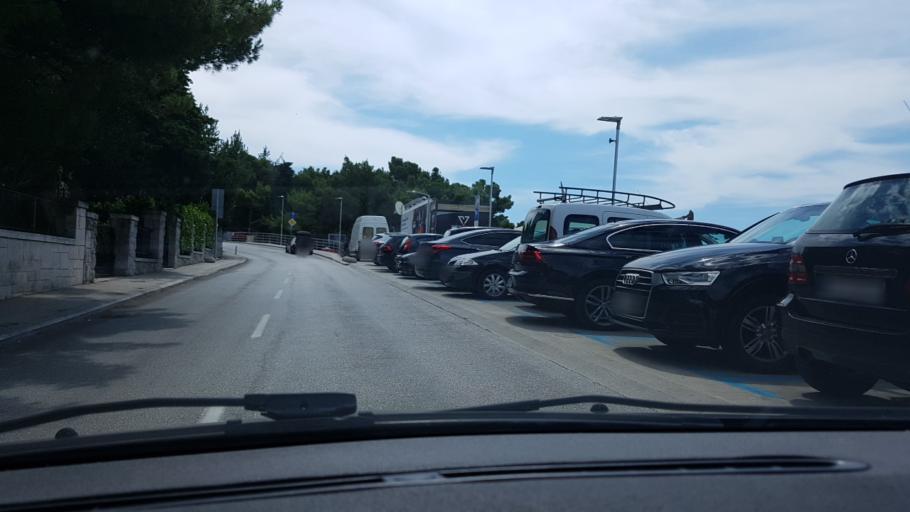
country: HR
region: Splitsko-Dalmatinska
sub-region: Grad Split
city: Split
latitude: 43.5020
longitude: 16.4490
